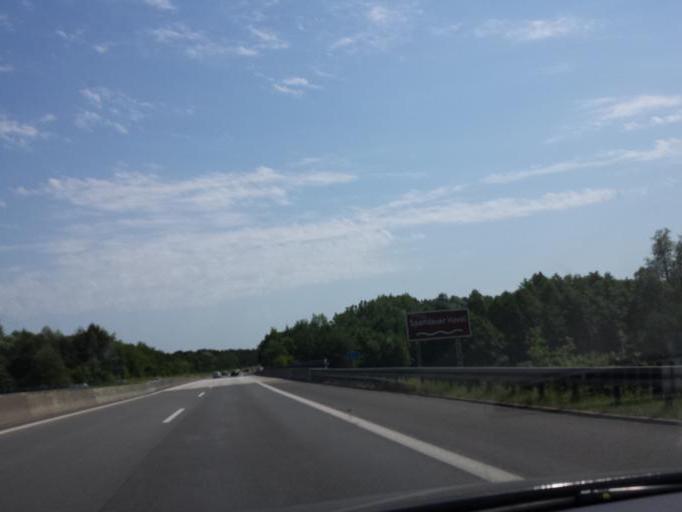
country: DE
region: Brandenburg
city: Hohen Neuendorf
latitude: 52.6734
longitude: 13.2334
